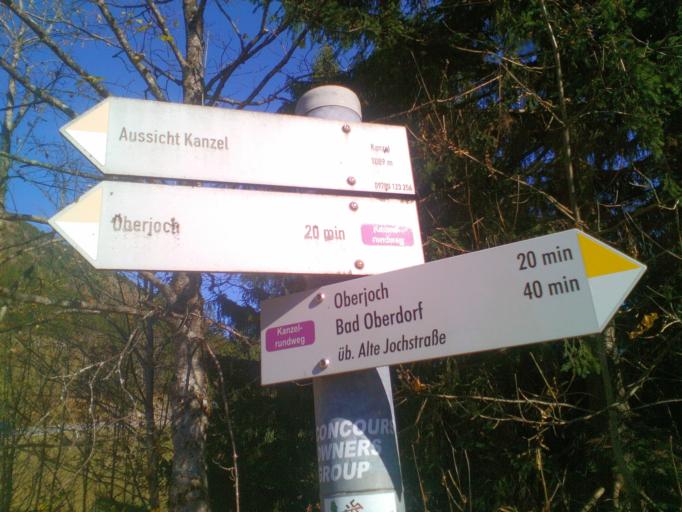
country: AT
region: Tyrol
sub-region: Politischer Bezirk Reutte
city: Schattwald
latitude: 47.5111
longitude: 10.3915
